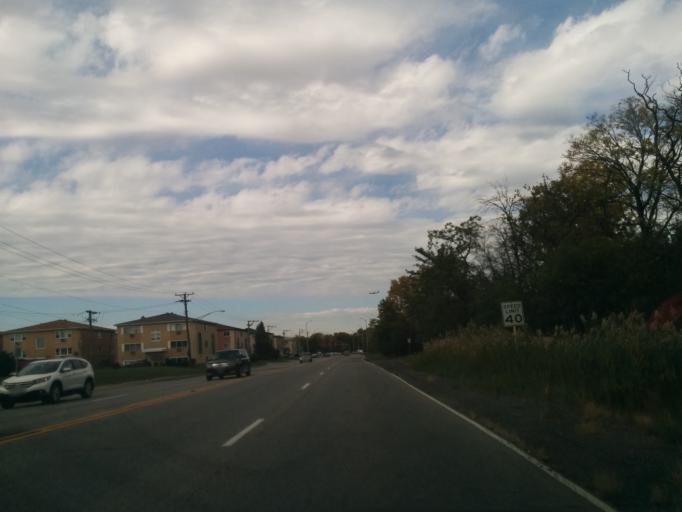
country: US
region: Illinois
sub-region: Cook County
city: Schiller Park
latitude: 41.9501
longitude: -87.8561
